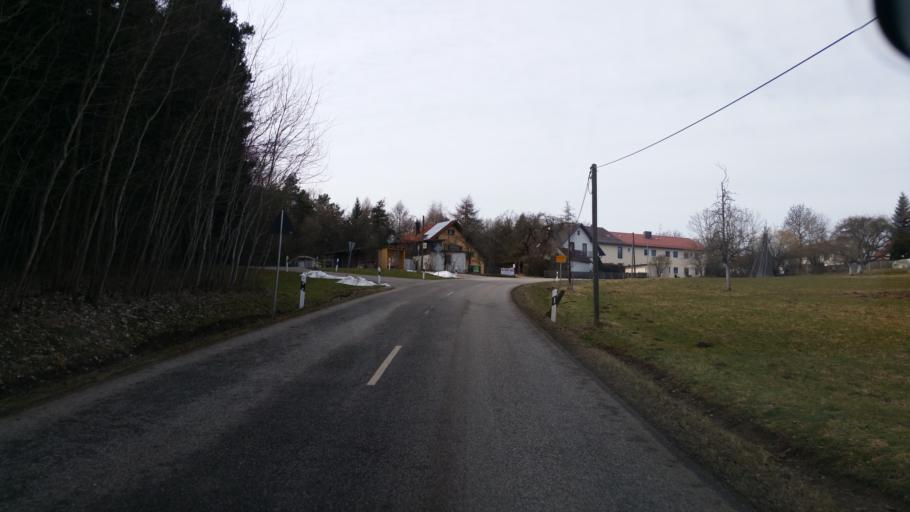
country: DE
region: Bavaria
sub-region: Lower Bavaria
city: Furth
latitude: 48.5791
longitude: 12.0191
